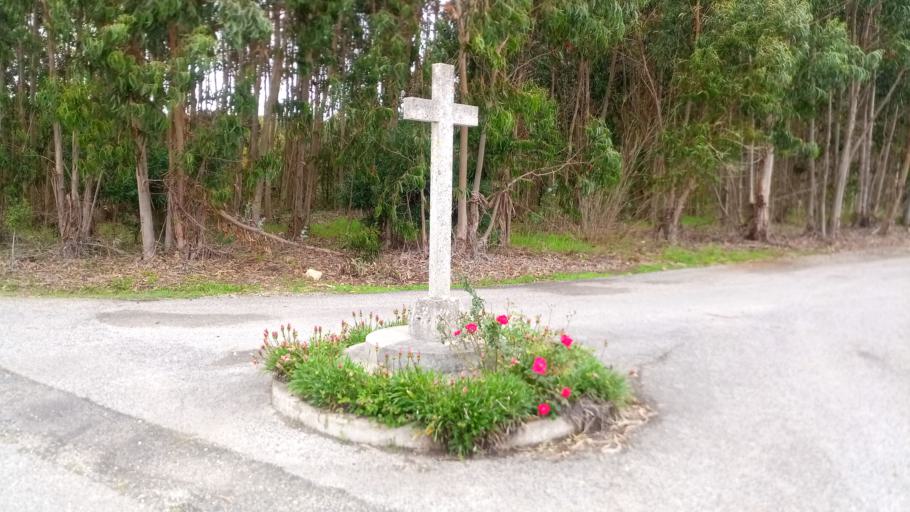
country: PT
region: Leiria
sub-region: Caldas da Rainha
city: Caldas da Rainha
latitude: 39.4550
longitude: -9.1835
